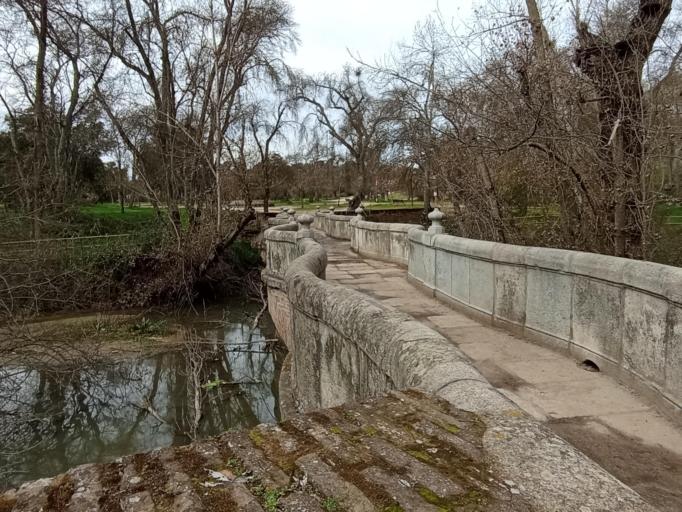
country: ES
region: Madrid
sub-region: Provincia de Madrid
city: Latina
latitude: 40.4019
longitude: -3.7718
